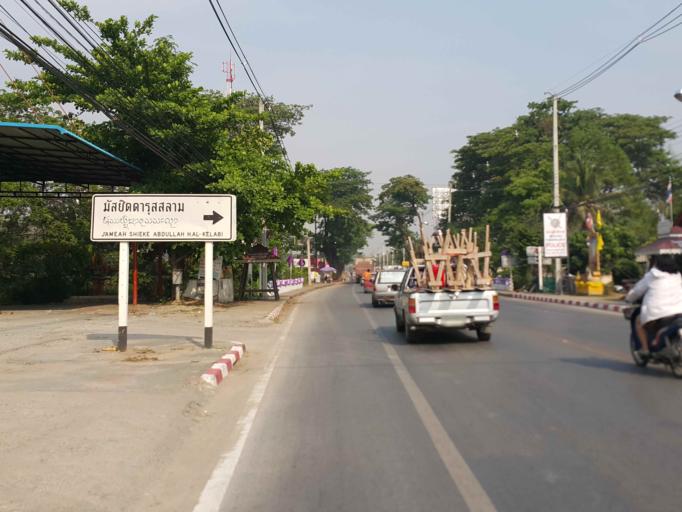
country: TH
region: Chiang Mai
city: Saraphi
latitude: 18.7749
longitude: 99.0608
